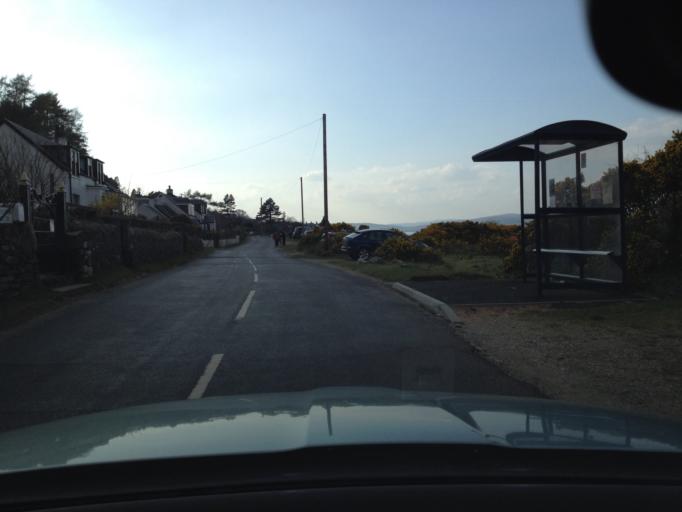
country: GB
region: Scotland
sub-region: North Ayrshire
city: Isle of Arran
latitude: 55.7042
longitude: -5.2925
